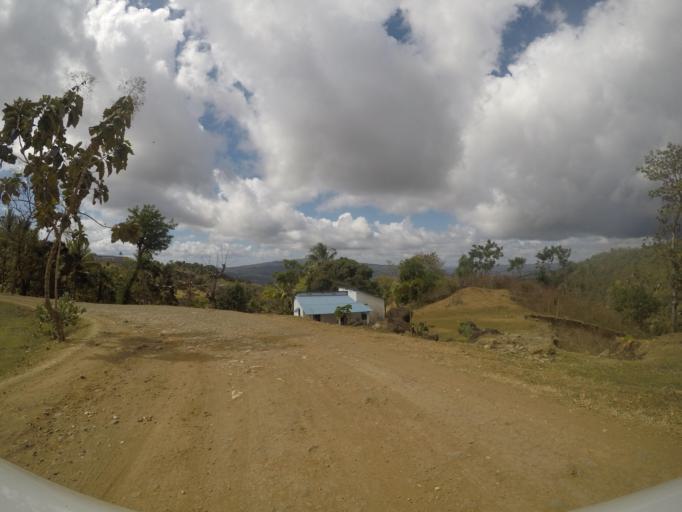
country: TL
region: Lautem
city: Lospalos
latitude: -8.5467
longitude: 126.8361
